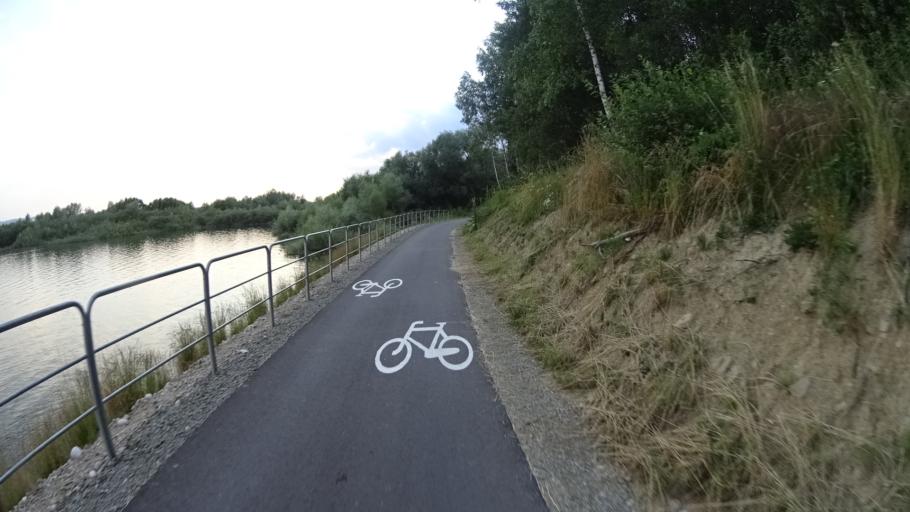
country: PL
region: Lesser Poland Voivodeship
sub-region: Powiat nowotarski
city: Frydman
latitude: 49.4659
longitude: 20.2302
